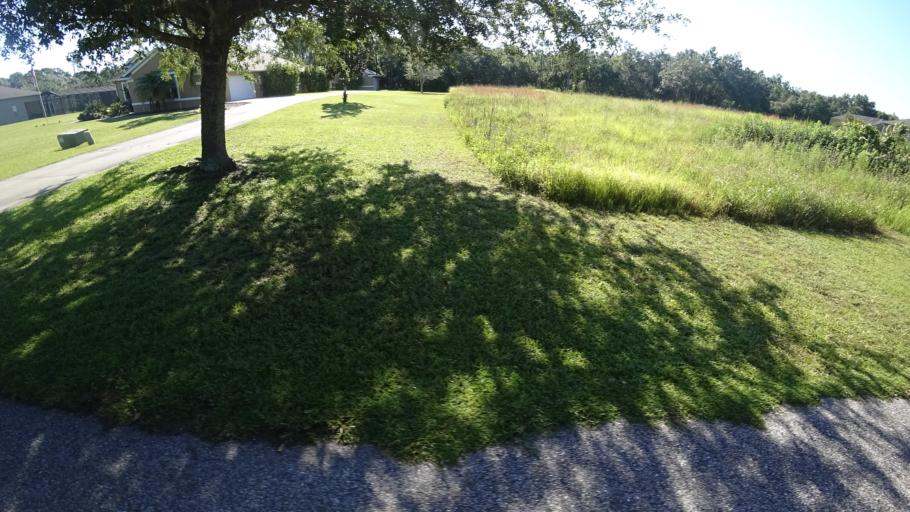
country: US
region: Florida
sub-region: Sarasota County
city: The Meadows
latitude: 27.4042
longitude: -82.3108
